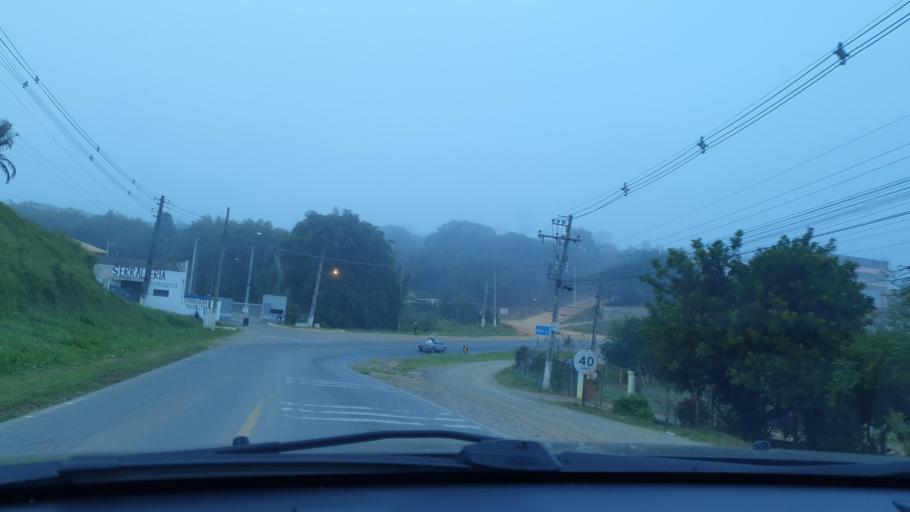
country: BR
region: Sao Paulo
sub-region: Ibiuna
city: Ibiuna
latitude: -23.6656
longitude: -47.2270
